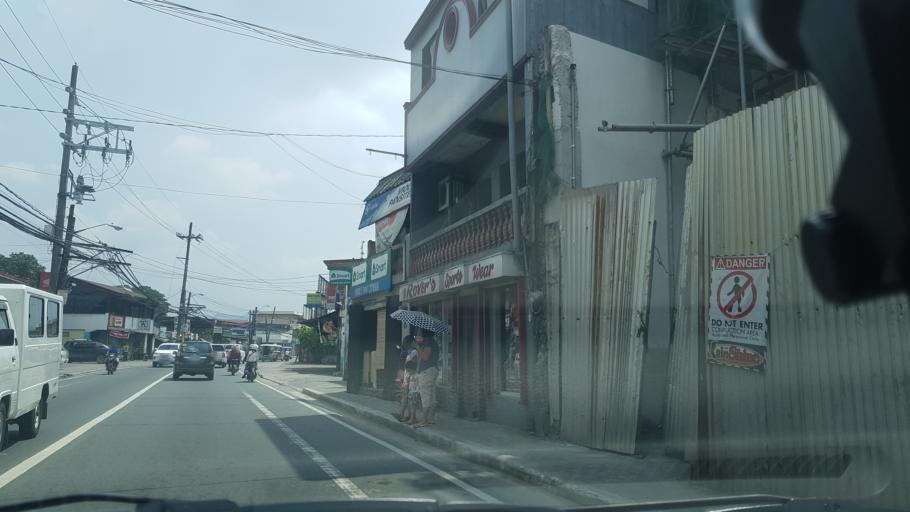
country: PH
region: Metro Manila
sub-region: Marikina
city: Calumpang
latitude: 14.6493
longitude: 121.0987
